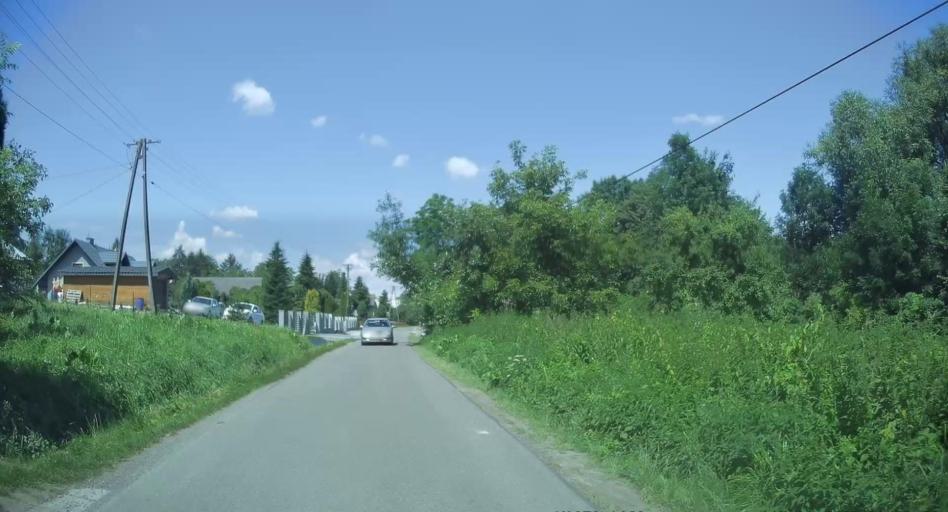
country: PL
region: Subcarpathian Voivodeship
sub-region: Powiat jaroslawski
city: Sosnica
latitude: 49.8628
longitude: 22.8795
